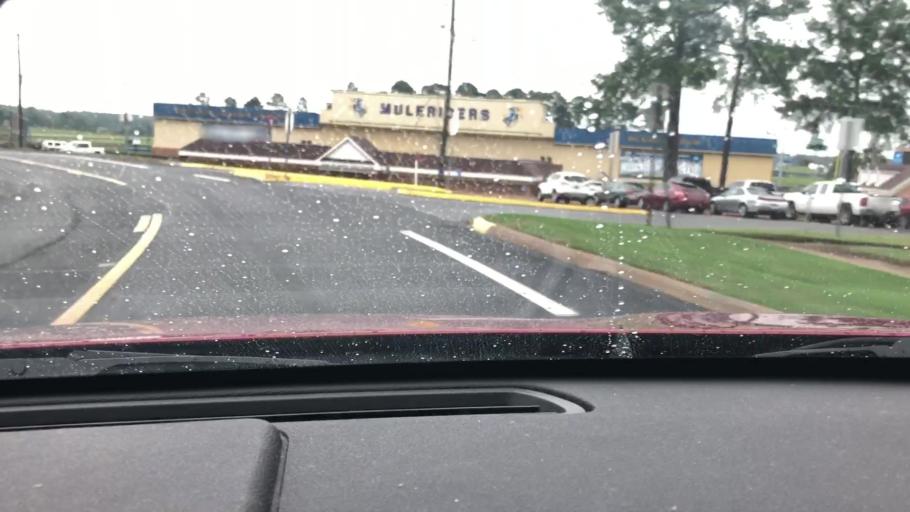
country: US
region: Arkansas
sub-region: Columbia County
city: Magnolia
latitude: 33.2938
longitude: -93.2362
